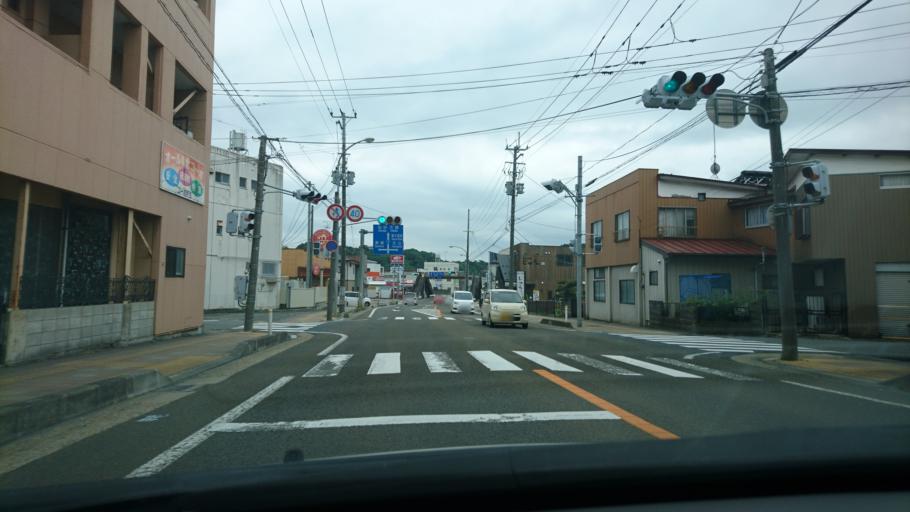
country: JP
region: Miyagi
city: Furukawa
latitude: 38.7324
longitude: 141.0227
